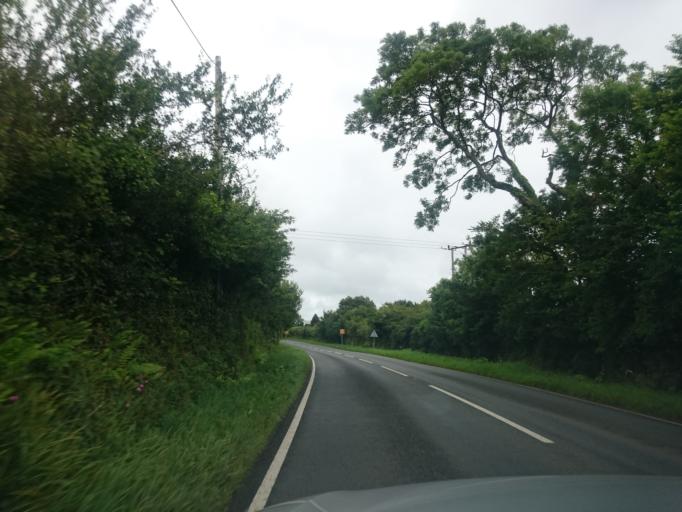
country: GB
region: Wales
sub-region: Pembrokeshire
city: Freystrop
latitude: 51.7754
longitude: -4.9663
